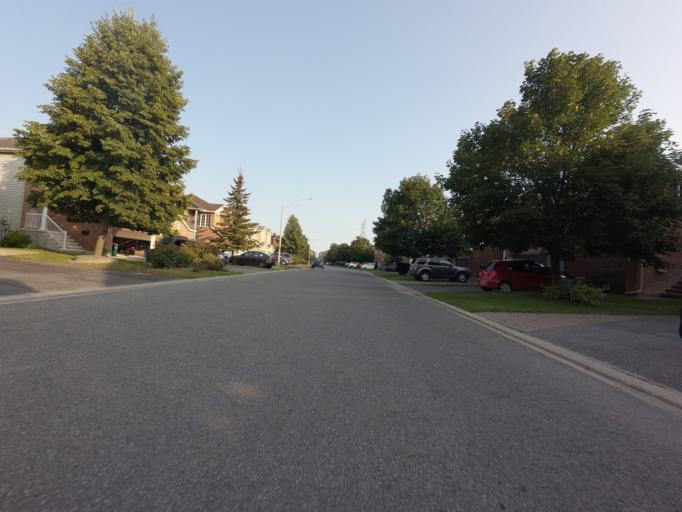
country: CA
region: Ontario
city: Bells Corners
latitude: 45.2847
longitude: -75.8844
